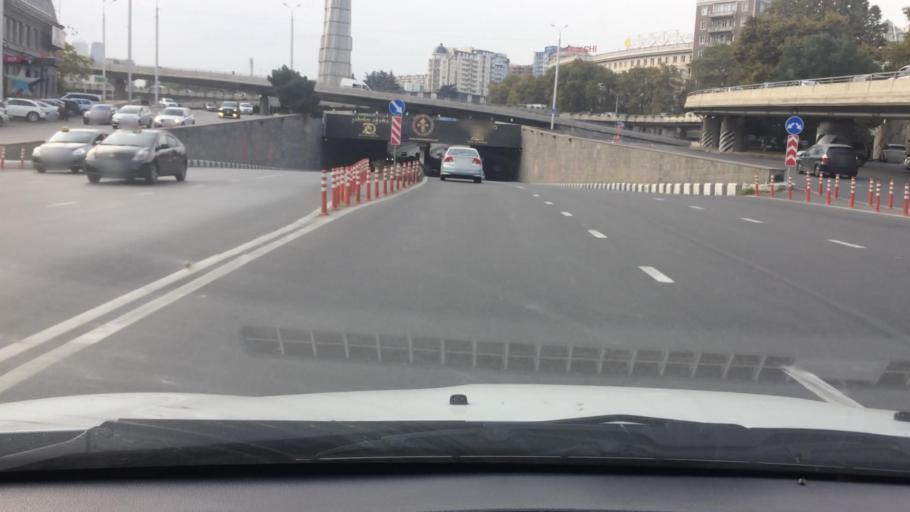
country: GE
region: T'bilisi
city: Tbilisi
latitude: 41.7127
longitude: 44.7849
